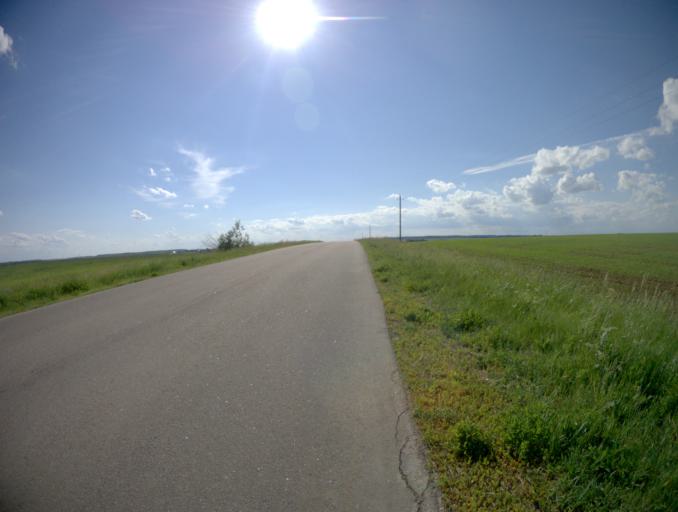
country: RU
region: Vladimir
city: Suzdal'
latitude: 56.3415
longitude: 40.4673
